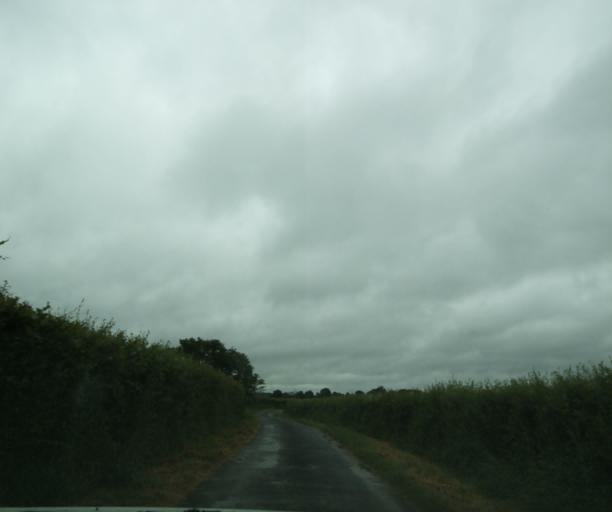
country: FR
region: Bourgogne
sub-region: Departement de Saone-et-Loire
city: Palinges
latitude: 46.5580
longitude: 4.2001
